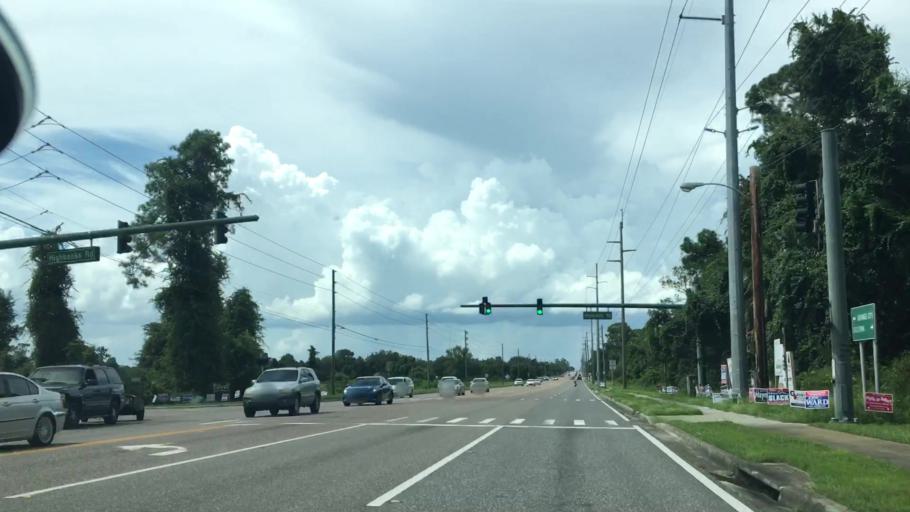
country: US
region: Florida
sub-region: Volusia County
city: Deltona
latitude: 28.8902
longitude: -81.2809
